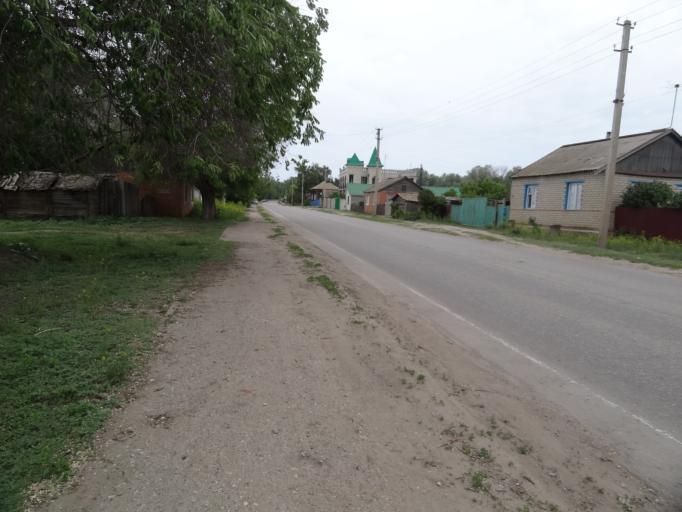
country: RU
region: Saratov
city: Privolzhskiy
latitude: 51.1875
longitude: 45.9164
